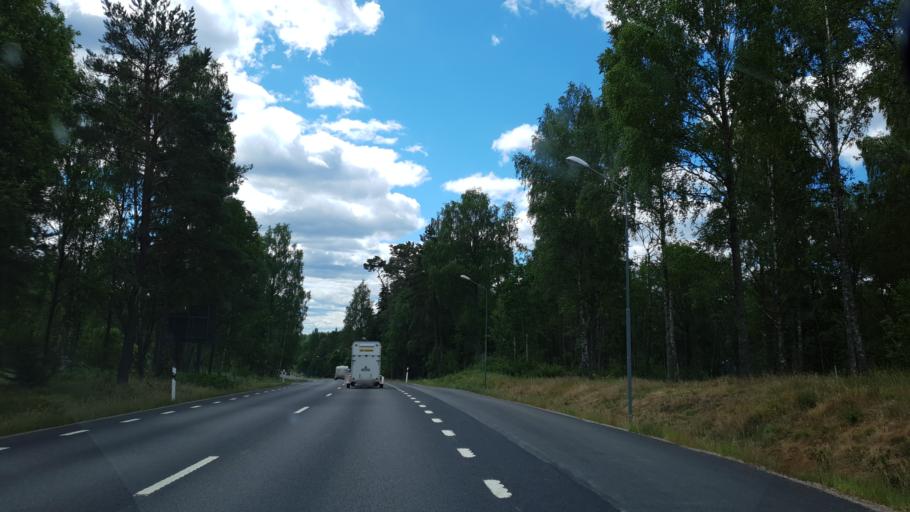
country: SE
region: Kronoberg
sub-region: Vaxjo Kommun
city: Braas
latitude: 57.2262
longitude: 15.1443
